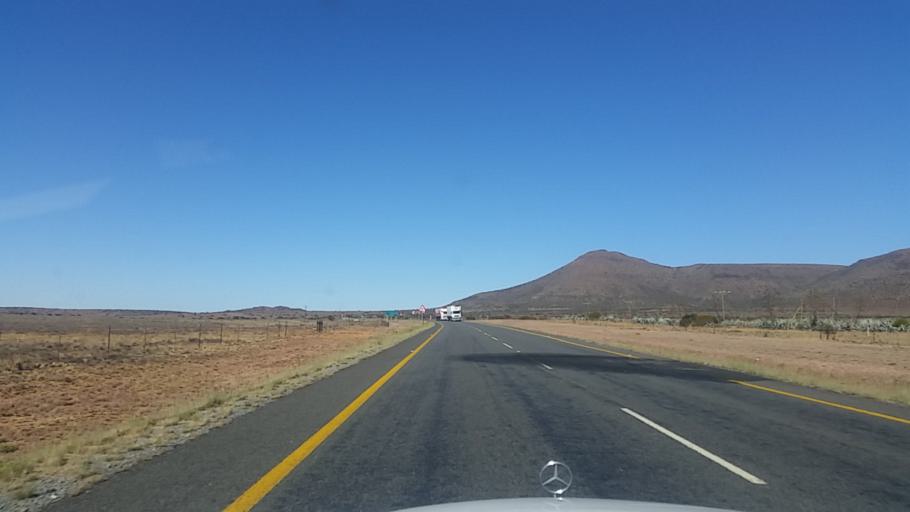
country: ZA
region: Eastern Cape
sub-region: Cacadu District Municipality
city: Graaff-Reinet
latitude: -32.0277
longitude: 24.6298
